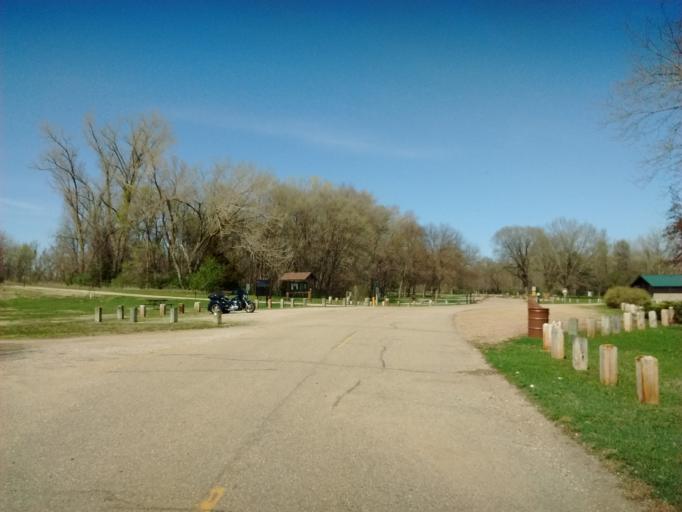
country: US
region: Iowa
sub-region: Plymouth County
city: Kingsley
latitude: 42.4517
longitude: -95.7970
